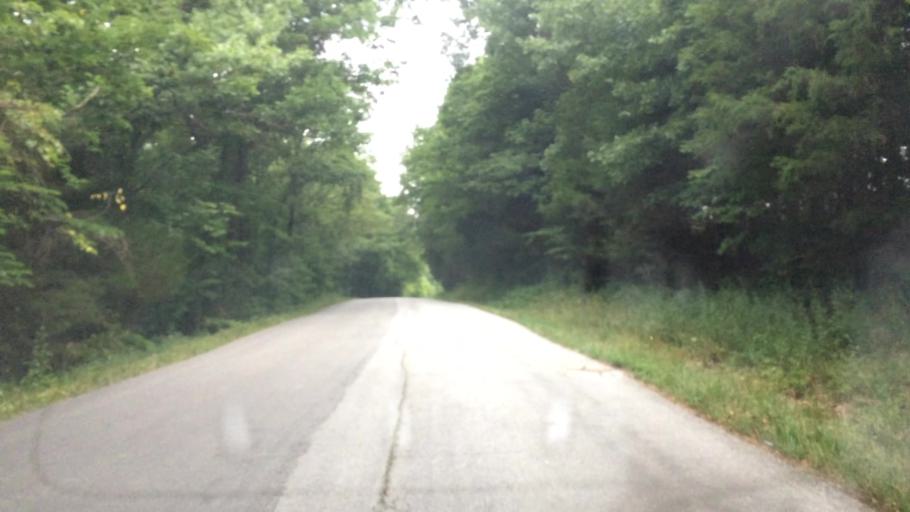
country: US
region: Missouri
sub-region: Greene County
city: Strafford
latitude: 37.3104
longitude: -93.0695
